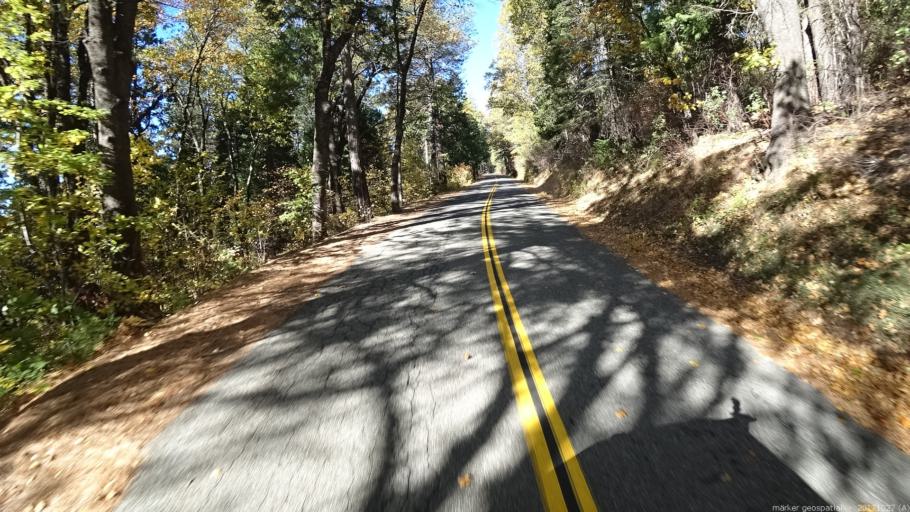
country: US
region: California
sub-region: Shasta County
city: Burney
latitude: 40.8603
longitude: -121.9112
